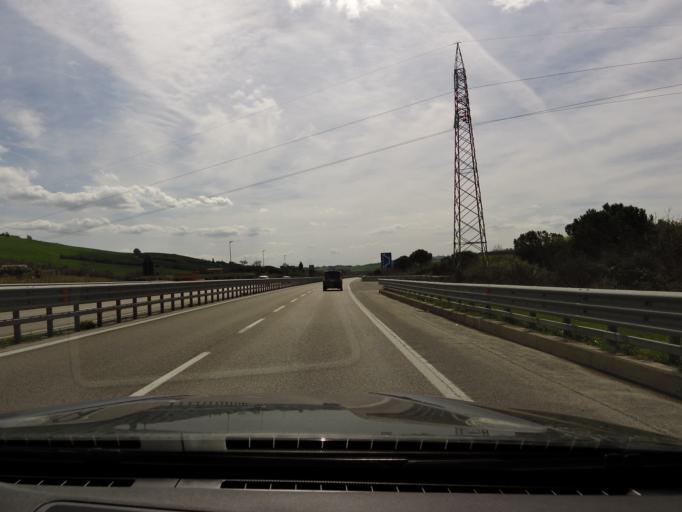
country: IT
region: The Marches
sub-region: Provincia di Ancona
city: San Biagio
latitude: 43.5533
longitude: 13.5175
